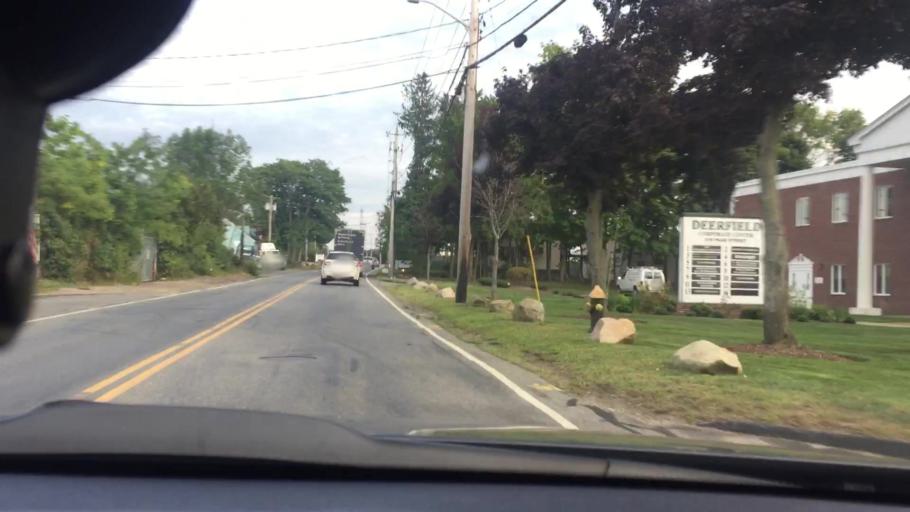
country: US
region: Massachusetts
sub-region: Norfolk County
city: Randolph
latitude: 42.1489
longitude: -71.0722
